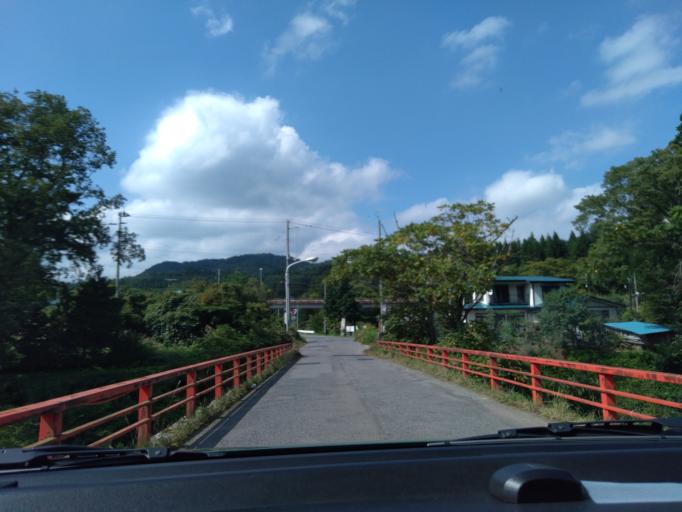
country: JP
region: Iwate
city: Shizukuishi
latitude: 39.6849
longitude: 140.9119
